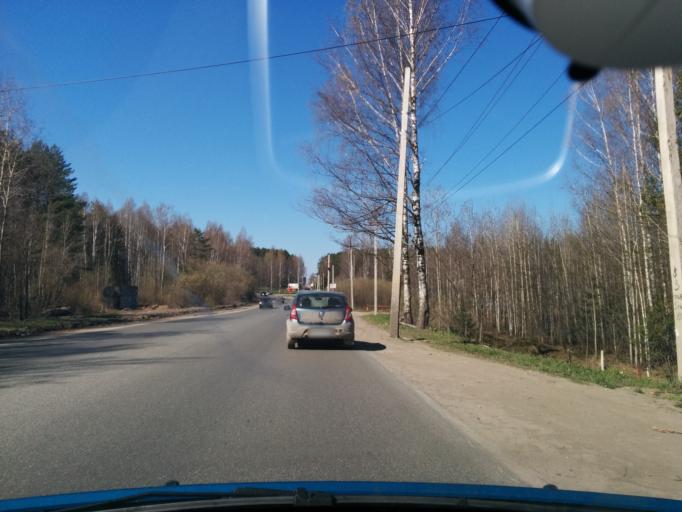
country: RU
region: Perm
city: Kondratovo
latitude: 58.0455
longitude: 56.0656
